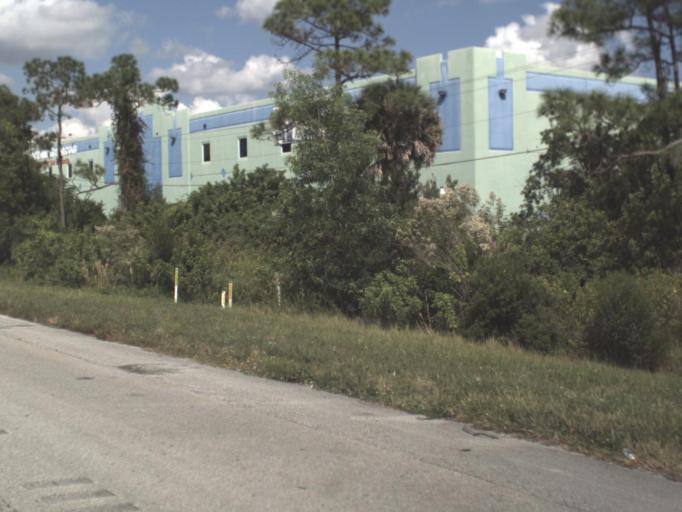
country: US
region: Florida
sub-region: Martin County
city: Palm City
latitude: 27.1071
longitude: -80.2671
